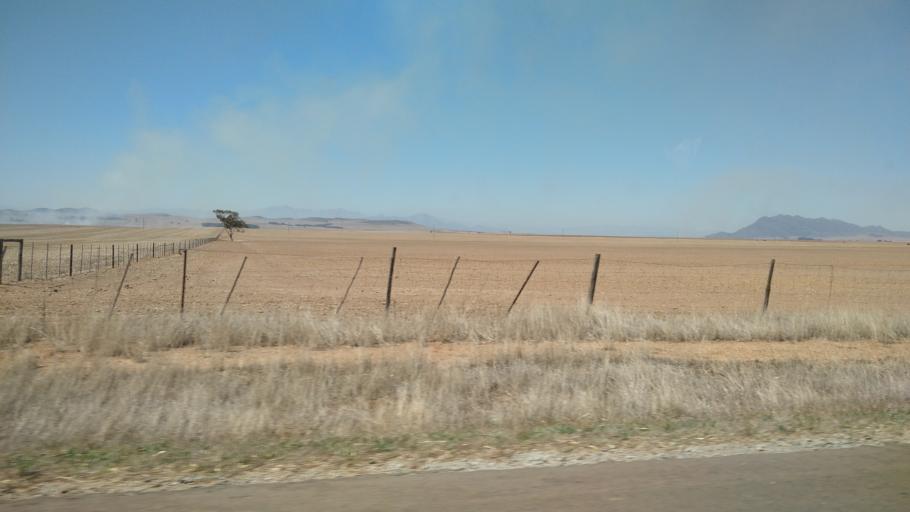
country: ZA
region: Western Cape
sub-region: West Coast District Municipality
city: Moorreesburg
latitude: -33.3082
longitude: 18.6184
